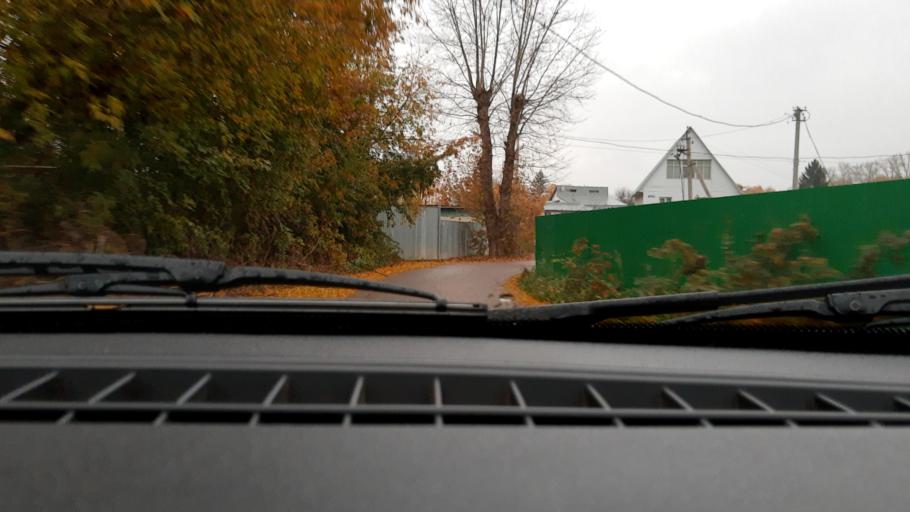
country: RU
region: Bashkortostan
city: Mikhaylovka
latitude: 54.7807
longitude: 55.8925
